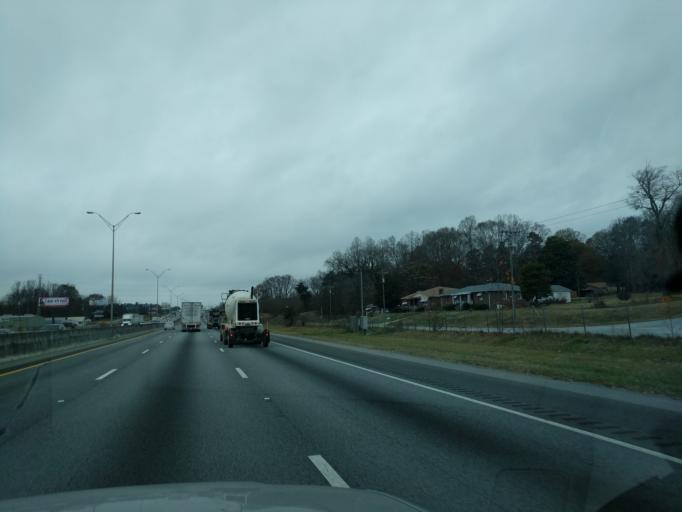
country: US
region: South Carolina
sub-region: Greenville County
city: Gantt
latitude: 34.7944
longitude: -82.3926
